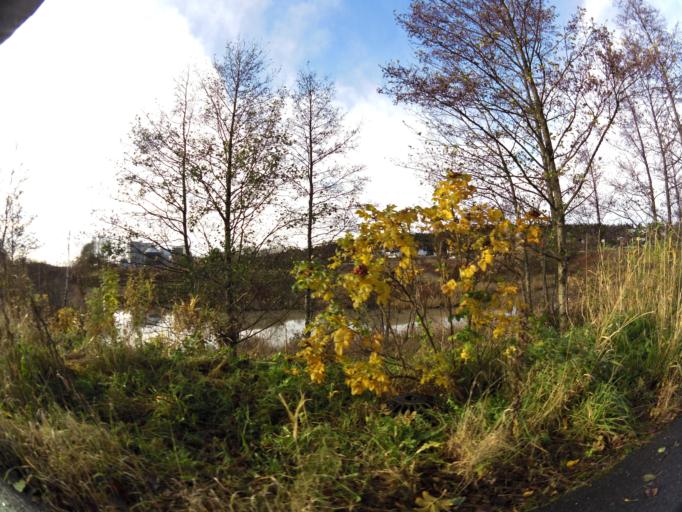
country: NO
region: Ostfold
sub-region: Sarpsborg
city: Sarpsborg
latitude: 59.2728
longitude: 11.0802
